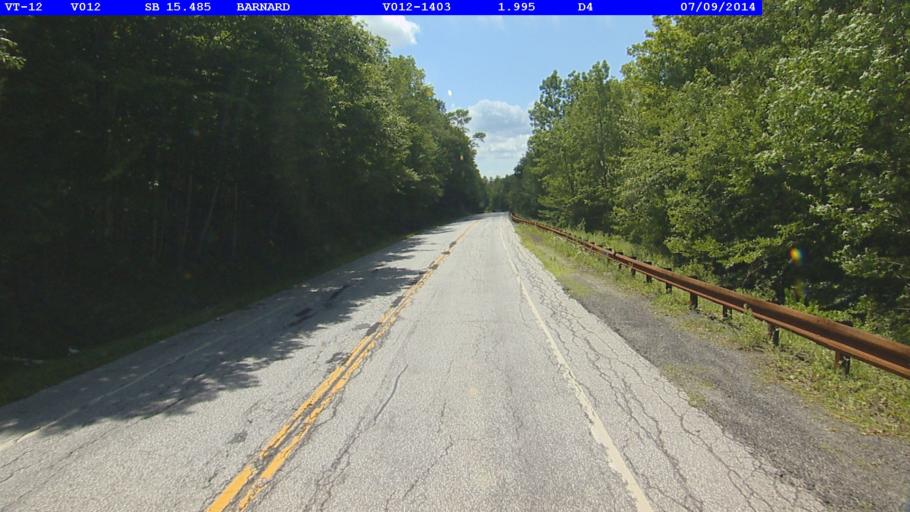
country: US
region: Vermont
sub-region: Windsor County
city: Woodstock
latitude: 43.6933
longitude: -72.6107
